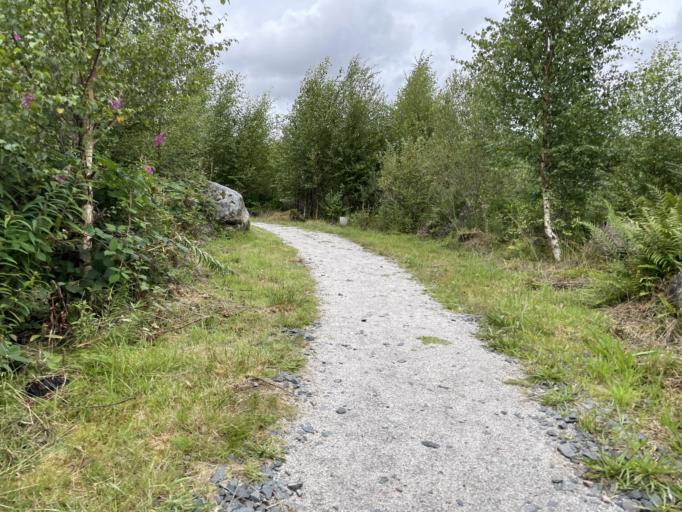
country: GB
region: Scotland
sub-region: Dumfries and Galloway
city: Newton Stewart
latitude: 55.0839
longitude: -4.5040
